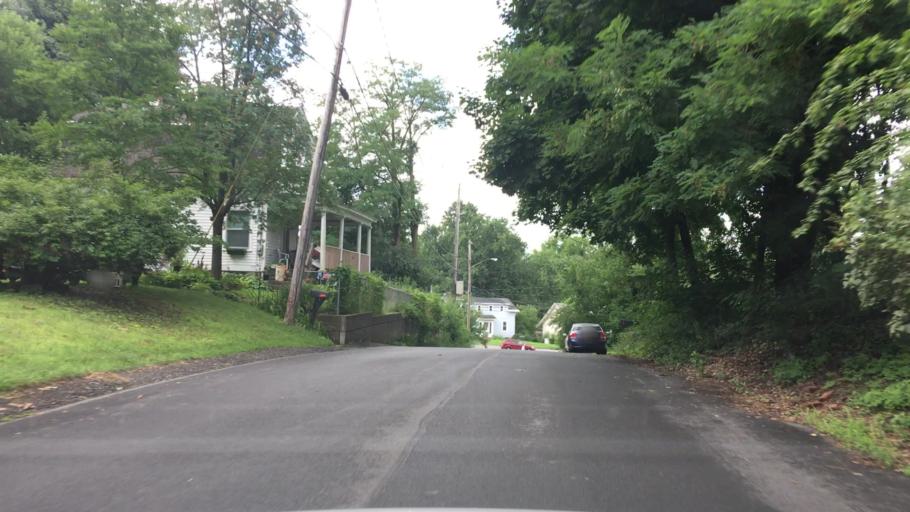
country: US
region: New York
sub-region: Schenectady County
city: Niskayuna
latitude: 42.7768
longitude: -73.8980
